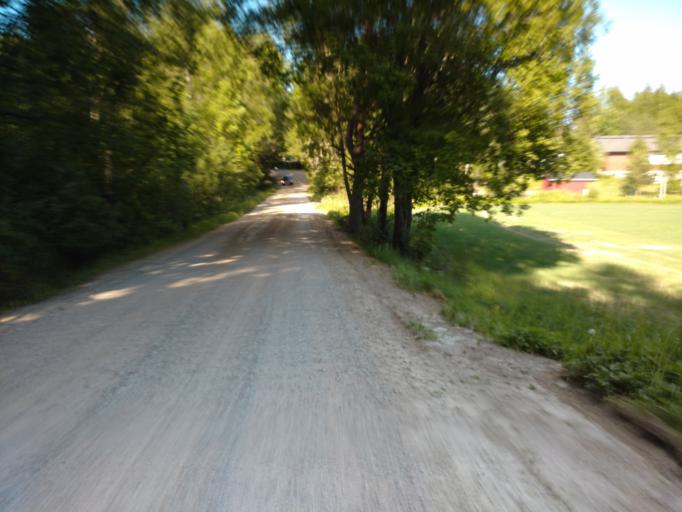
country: FI
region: Varsinais-Suomi
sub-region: Salo
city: Salo
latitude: 60.3589
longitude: 23.1813
